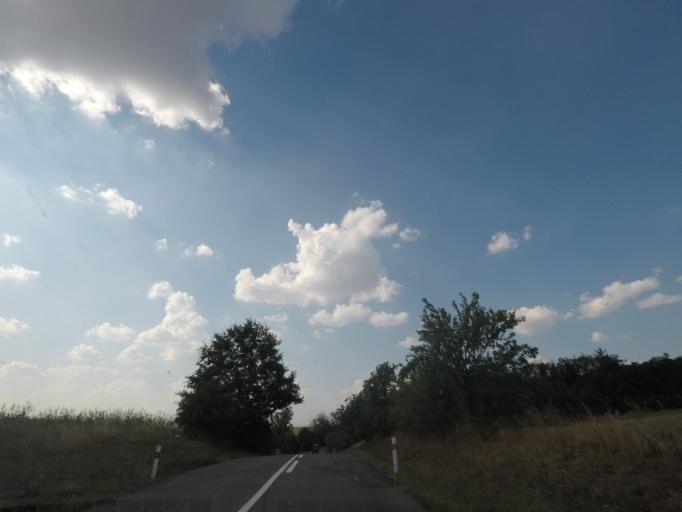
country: CZ
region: Kralovehradecky
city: Trebechovice pod Orebem
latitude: 50.2237
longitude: 15.9741
